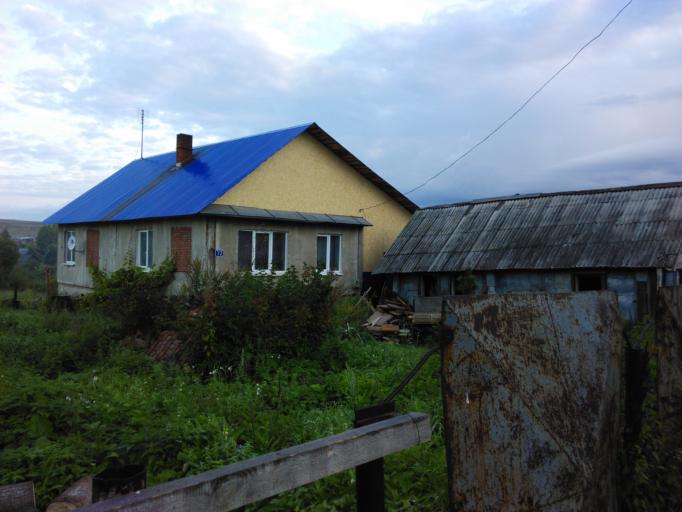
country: RU
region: Perm
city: Foki
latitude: 56.6947
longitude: 54.3507
